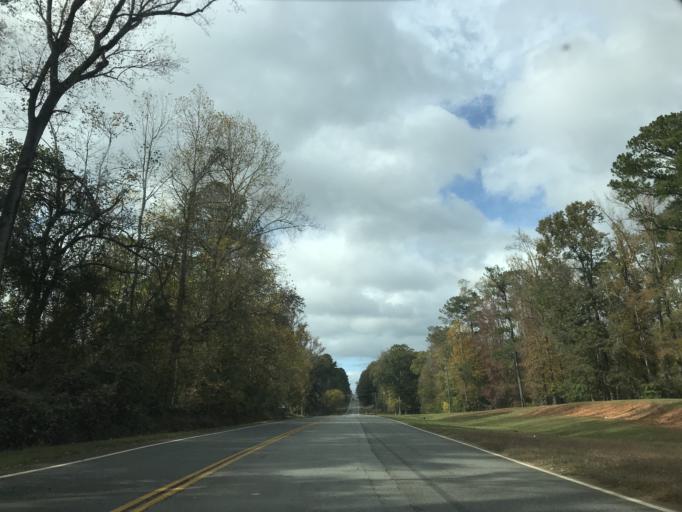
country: US
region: Georgia
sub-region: Jones County
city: Gray
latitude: 32.9738
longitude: -83.5007
